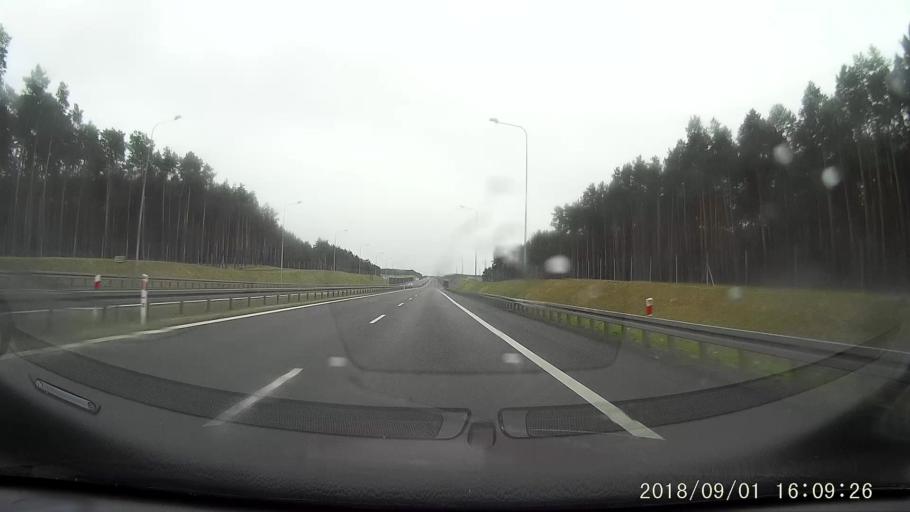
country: PL
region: Lubusz
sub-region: Powiat miedzyrzecki
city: Skwierzyna
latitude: 52.5510
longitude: 15.5394
